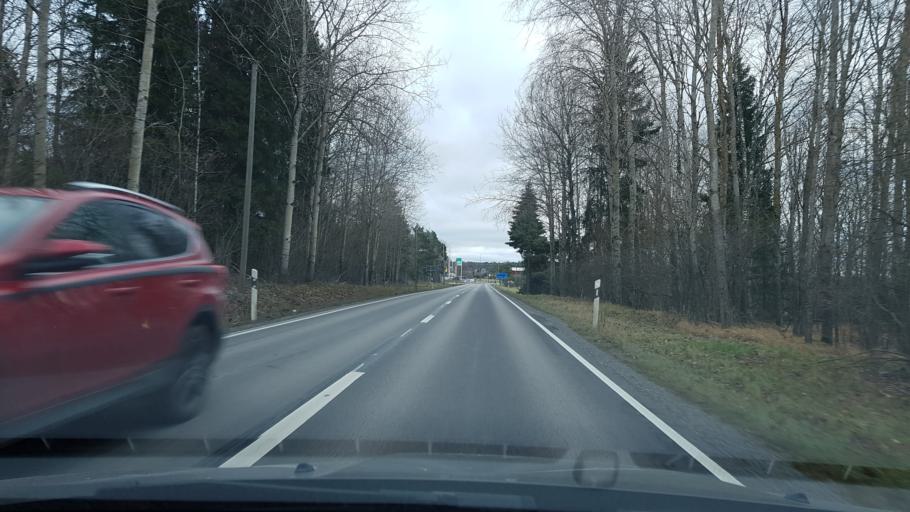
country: SE
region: Stockholm
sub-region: Norrtalje Kommun
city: Hallstavik
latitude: 60.0418
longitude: 18.5461
